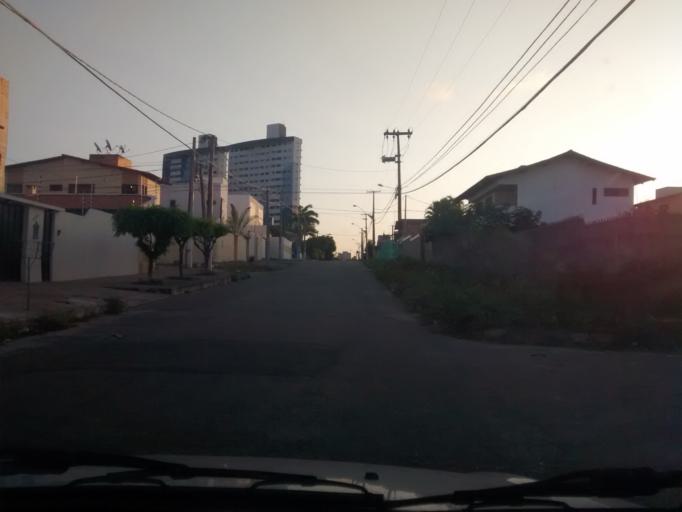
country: BR
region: Rio Grande do Norte
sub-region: Natal
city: Natal
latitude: -5.8699
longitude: -35.1889
